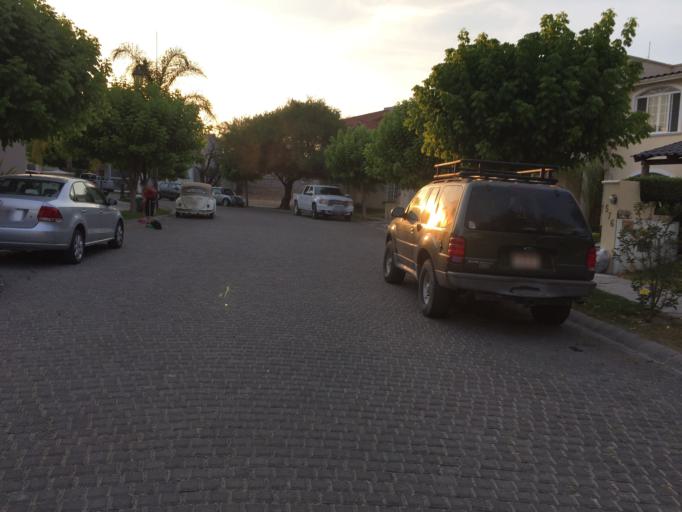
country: MX
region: Aguascalientes
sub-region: Aguascalientes
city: La Loma de los Negritos
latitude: 21.8532
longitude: -102.3558
